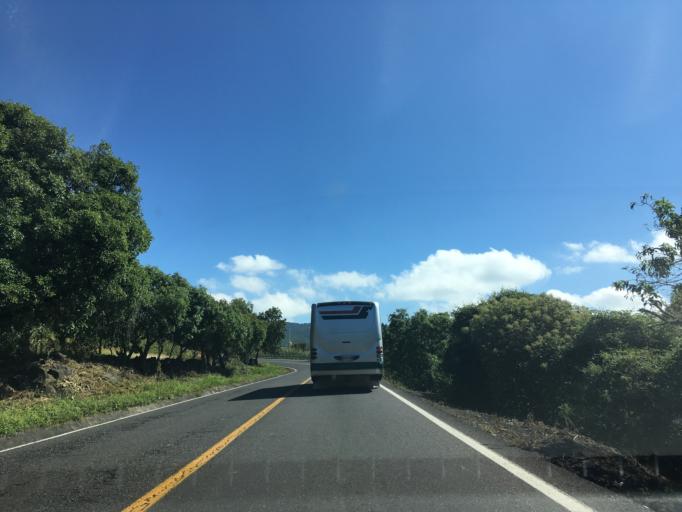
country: MX
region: Mexico
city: Tlazazalca
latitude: 20.0316
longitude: -102.0638
